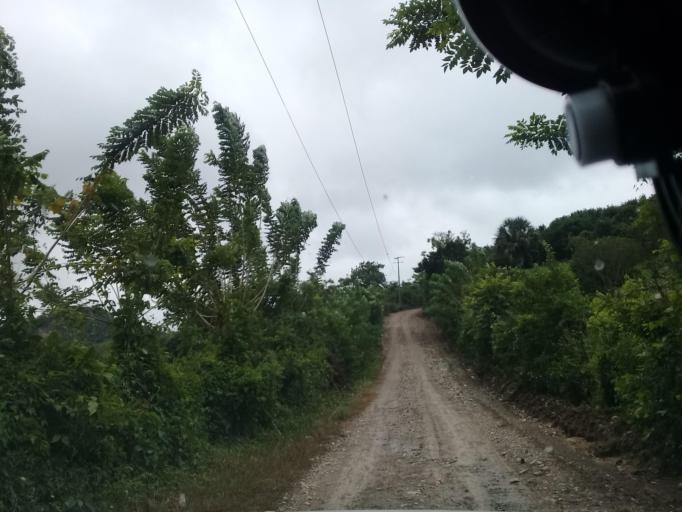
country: MX
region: Veracruz
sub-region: Chalma
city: San Pedro Coyutla
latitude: 21.2414
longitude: -98.4184
